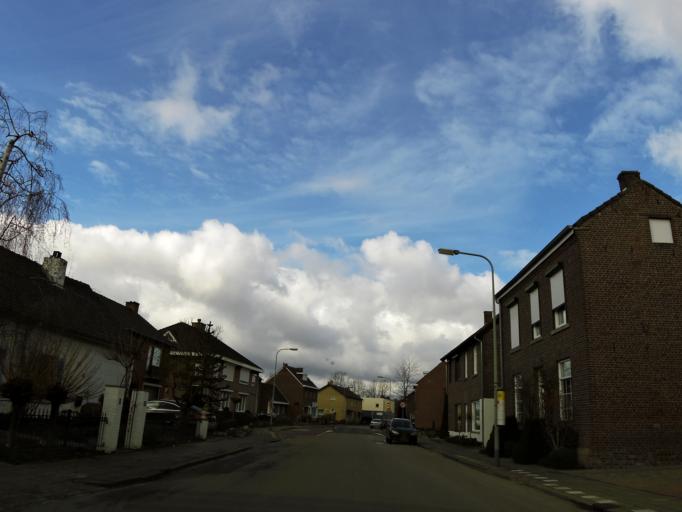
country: NL
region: Limburg
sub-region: Gemeente Meerssen
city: Meerssen
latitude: 50.8968
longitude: 5.7058
